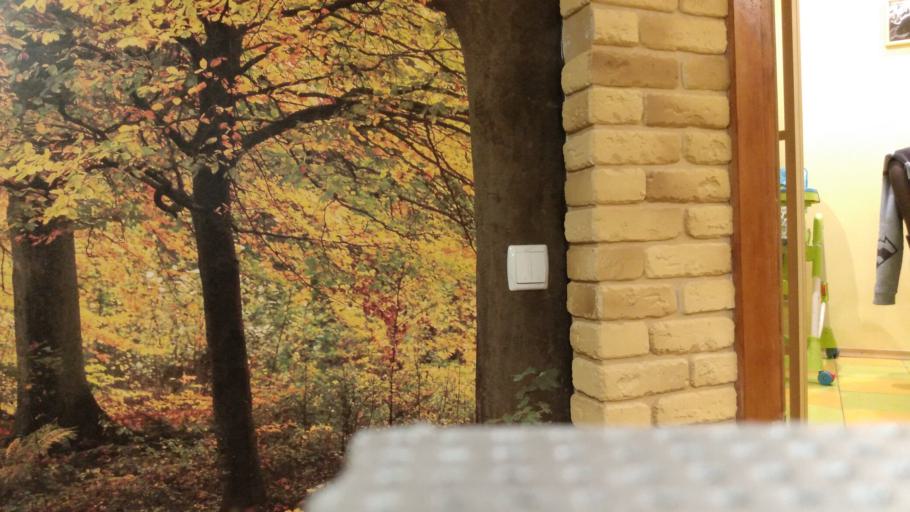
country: RU
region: Vologda
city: Babayevo
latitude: 59.3693
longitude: 35.9959
